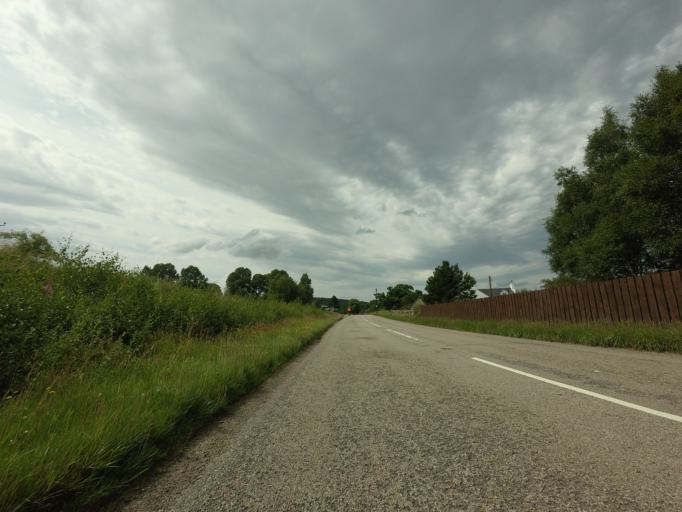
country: GB
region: Scotland
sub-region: Highland
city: Alness
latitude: 57.8711
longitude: -4.3484
